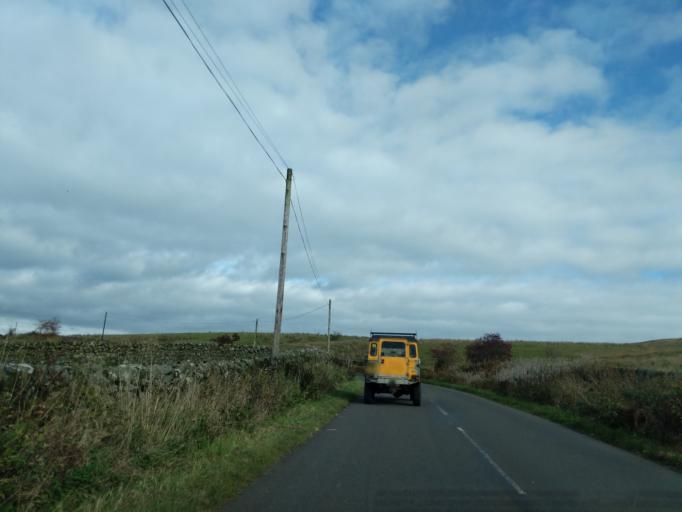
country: GB
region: Scotland
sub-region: Dumfries and Galloway
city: Thornhill
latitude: 55.1963
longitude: -3.8498
